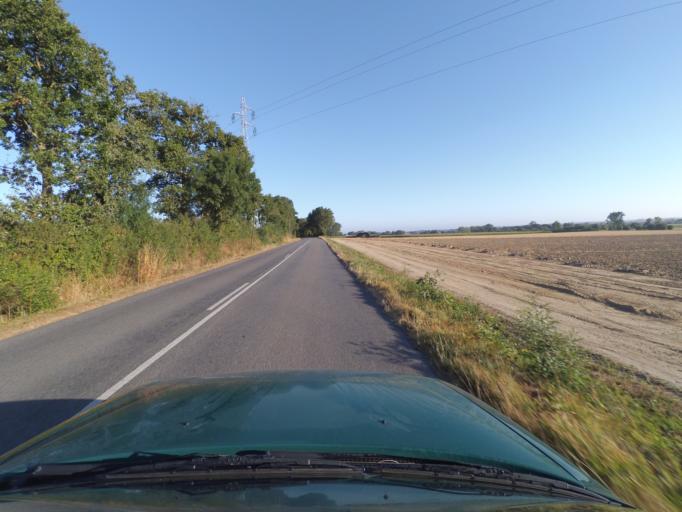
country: FR
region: Pays de la Loire
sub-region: Departement de la Loire-Atlantique
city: Vieillevigne
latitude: 46.9932
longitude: -1.4505
